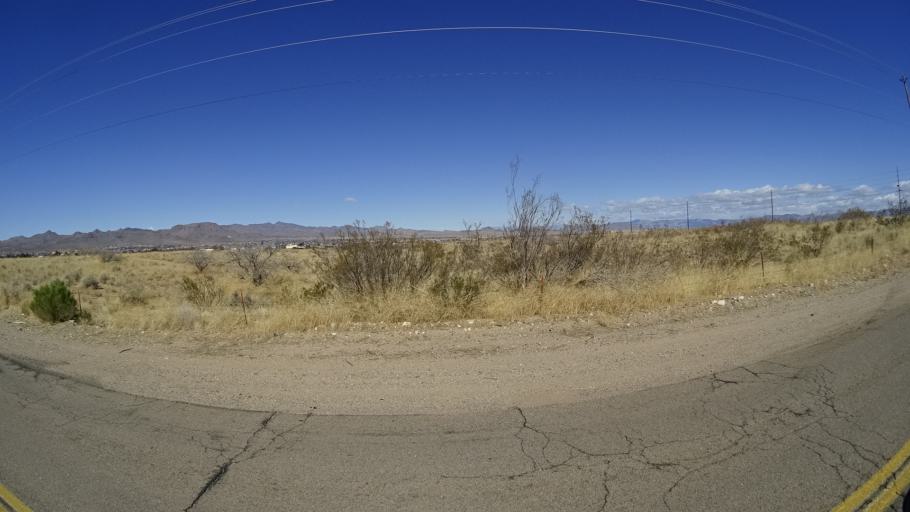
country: US
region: Arizona
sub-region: Mohave County
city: Kingman
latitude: 35.1998
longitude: -113.9905
